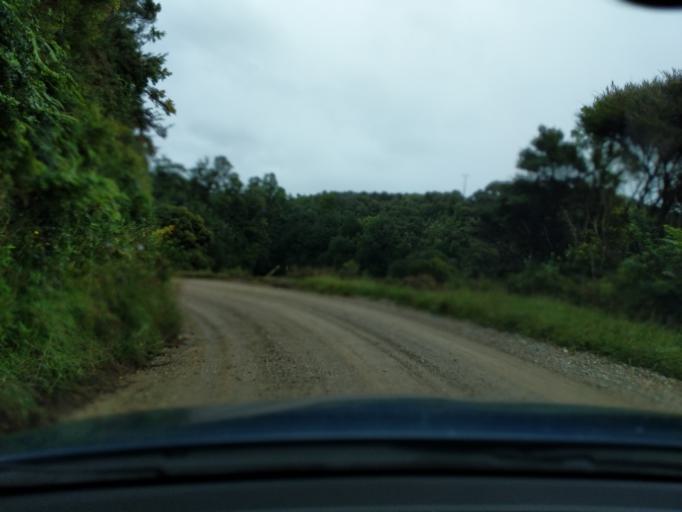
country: NZ
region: Tasman
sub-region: Tasman District
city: Takaka
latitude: -40.6253
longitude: 172.5186
